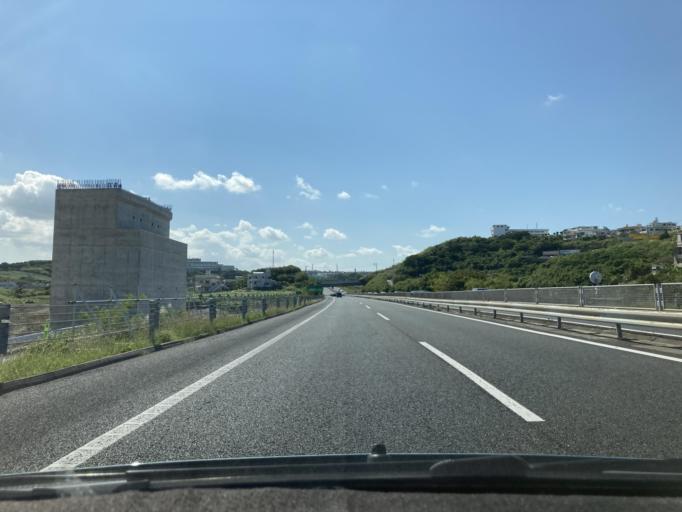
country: JP
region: Okinawa
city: Ginowan
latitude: 26.2375
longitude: 127.7411
